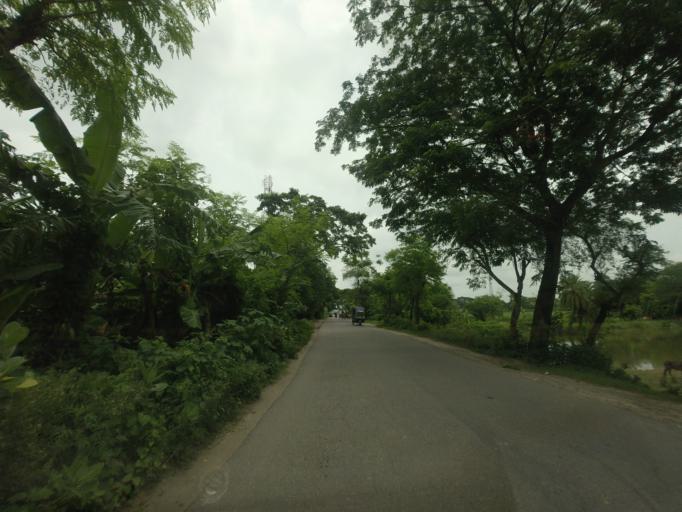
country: BD
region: Khulna
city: Kalia
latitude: 23.2112
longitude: 89.7092
